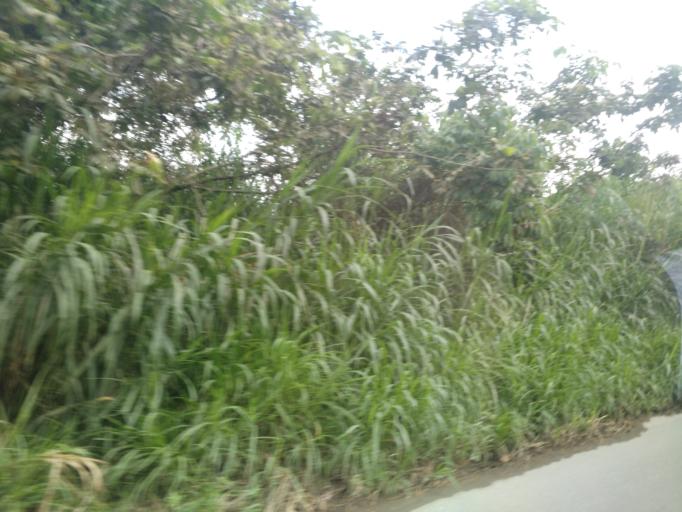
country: CO
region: Valle del Cauca
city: Sevilla
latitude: 4.2926
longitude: -75.9001
